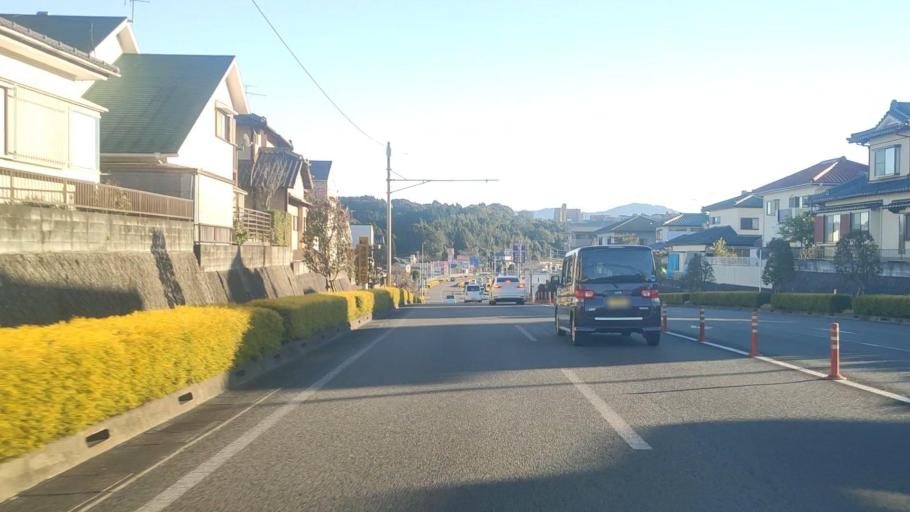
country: JP
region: Miyazaki
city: Miyazaki-shi
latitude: 31.8742
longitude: 131.3922
